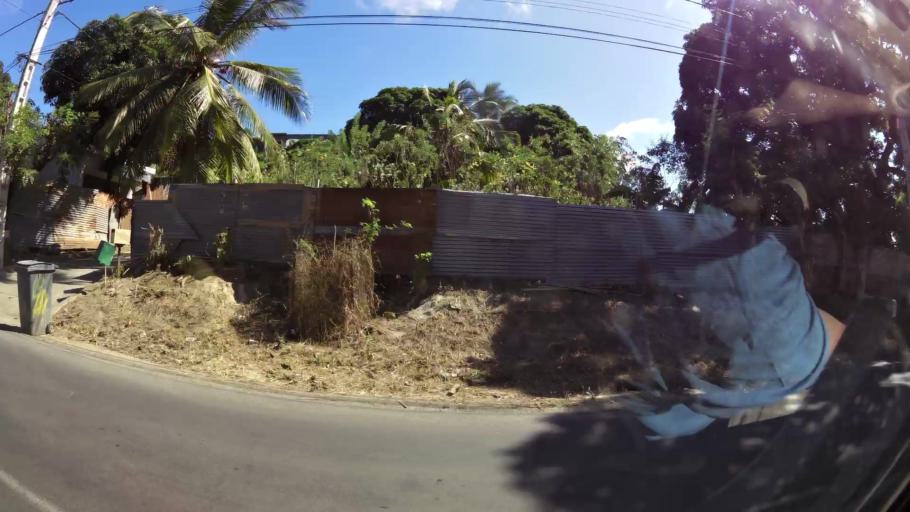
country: YT
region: Pamandzi
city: Pamandzi
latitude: -12.7820
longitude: 45.2797
